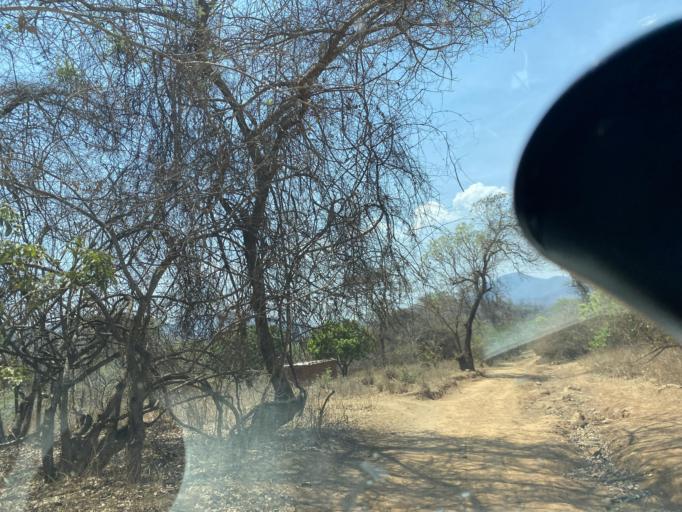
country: ZM
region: Lusaka
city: Kafue
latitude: -15.7919
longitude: 28.4559
